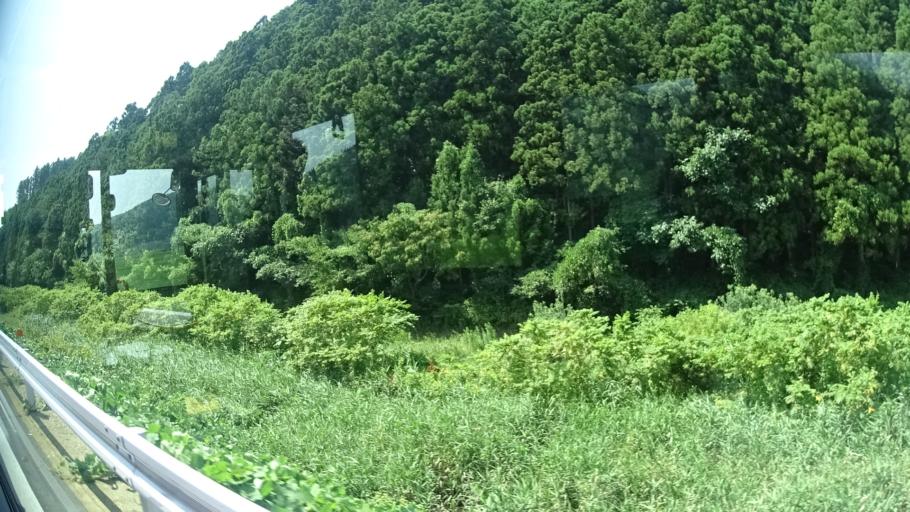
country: JP
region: Miyagi
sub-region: Oshika Gun
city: Onagawa Cho
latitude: 38.6276
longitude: 141.3379
